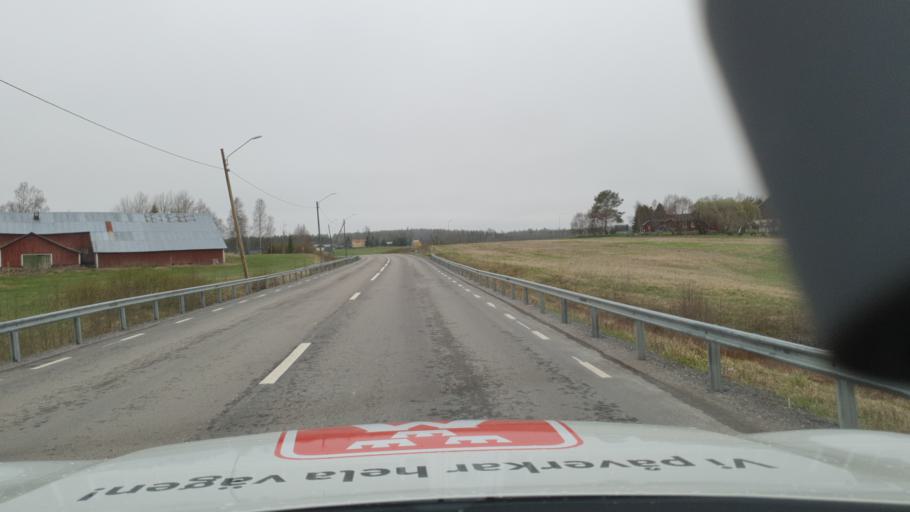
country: SE
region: Vaesterbotten
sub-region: Umea Kommun
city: Hoernefors
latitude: 63.7769
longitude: 19.9338
